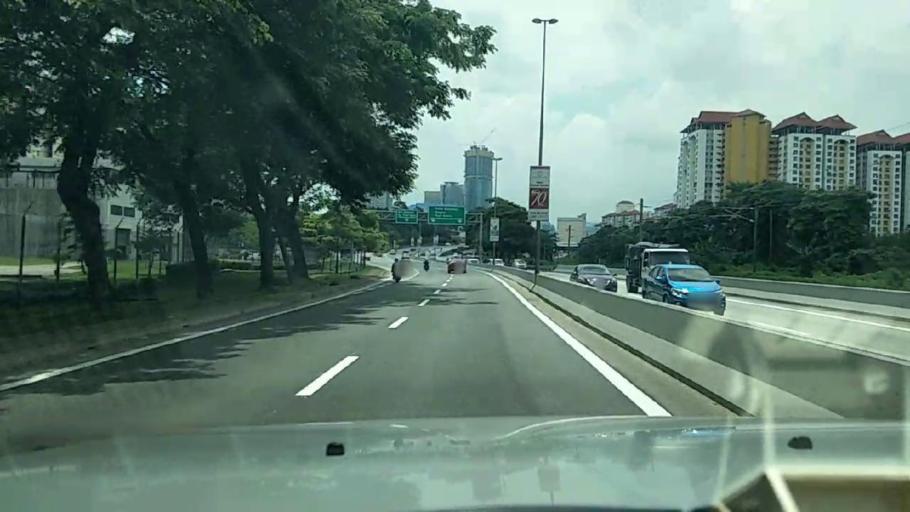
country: MY
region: Kuala Lumpur
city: Kuala Lumpur
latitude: 3.1032
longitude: 101.6719
